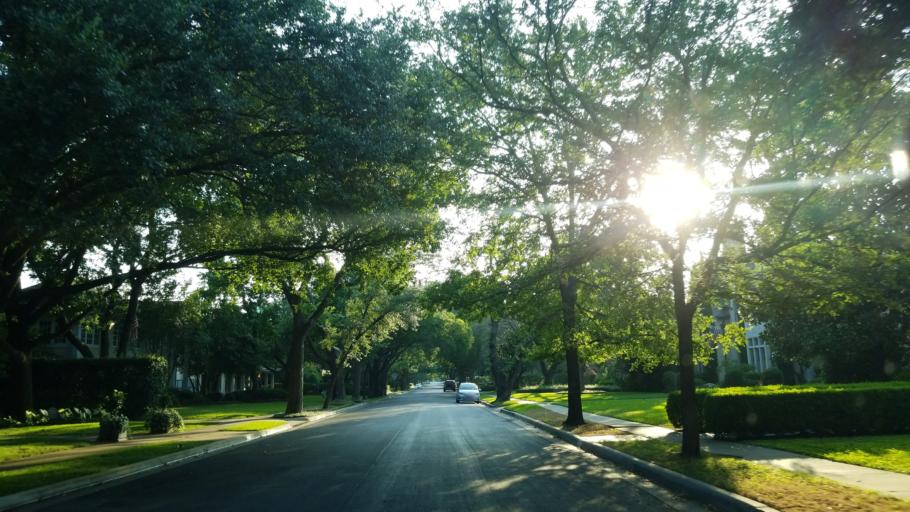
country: US
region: Texas
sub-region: Dallas County
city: Highland Park
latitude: 32.8378
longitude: -96.7944
